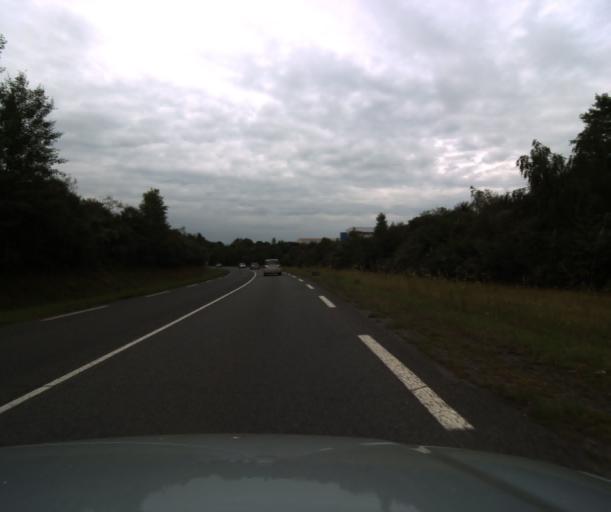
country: FR
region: Midi-Pyrenees
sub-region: Departement des Hautes-Pyrenees
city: Juillan
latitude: 43.1890
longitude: 0.0094
